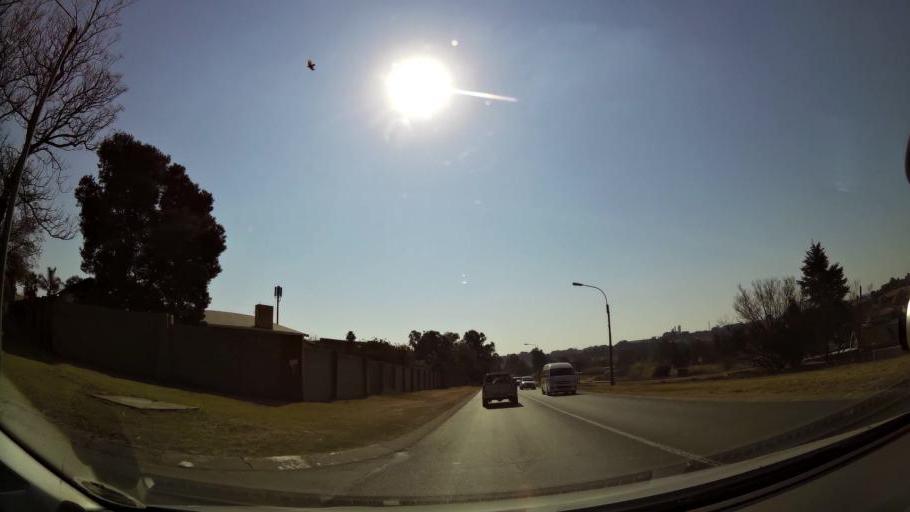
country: ZA
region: Gauteng
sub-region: City of Johannesburg Metropolitan Municipality
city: Modderfontein
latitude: -26.1095
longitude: 28.1683
